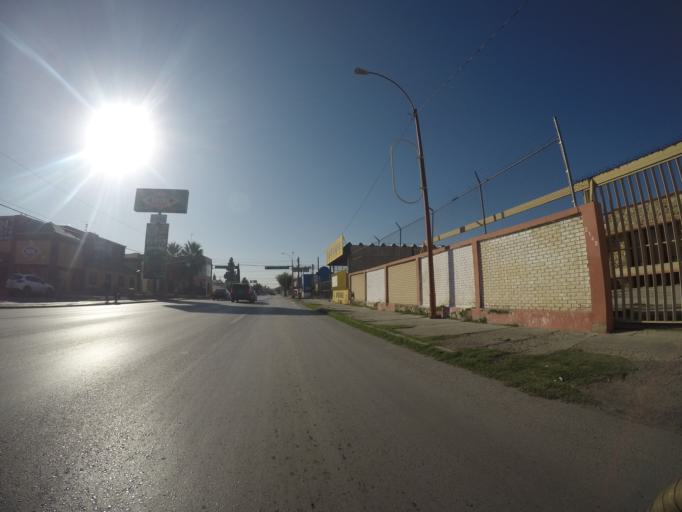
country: MX
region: Chihuahua
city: Ciudad Juarez
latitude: 31.7381
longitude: -106.4647
